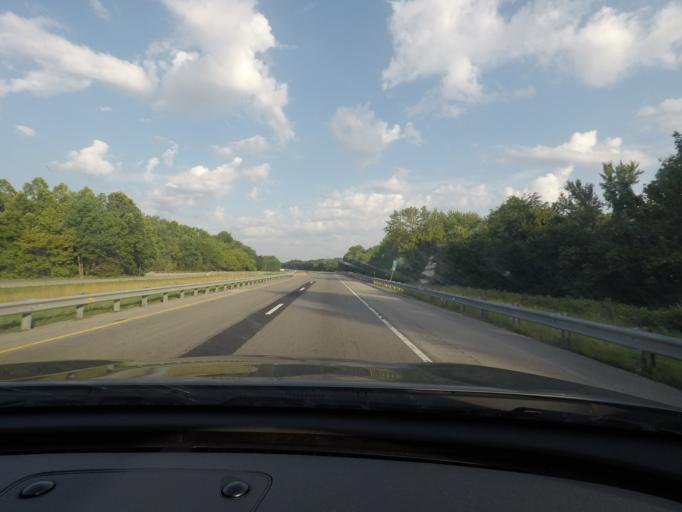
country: US
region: Illinois
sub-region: Jefferson County
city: Mount Vernon
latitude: 38.3607
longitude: -89.0124
